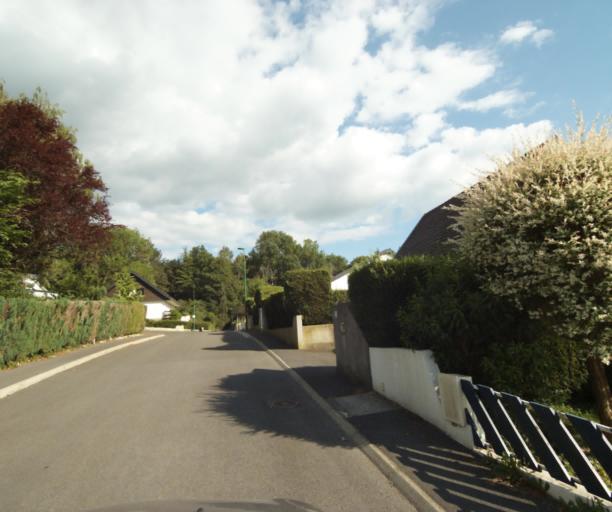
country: FR
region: Champagne-Ardenne
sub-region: Departement des Ardennes
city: Charleville-Mezieres
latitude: 49.7786
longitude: 4.7238
